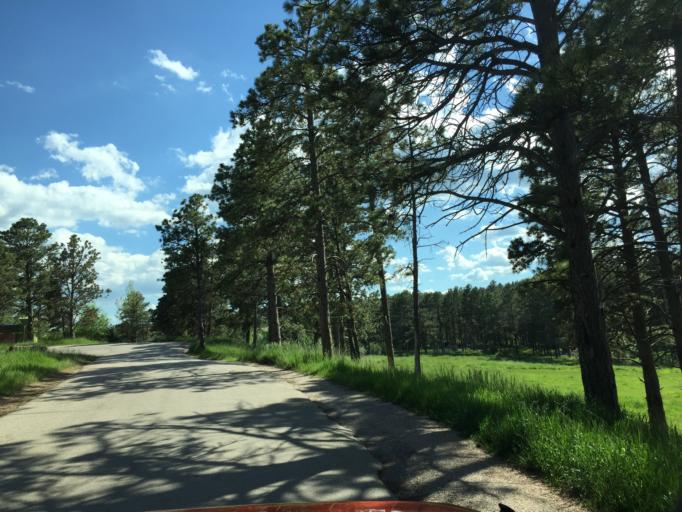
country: US
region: South Dakota
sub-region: Pennington County
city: Colonial Pine Hills
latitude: 43.9771
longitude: -103.3028
